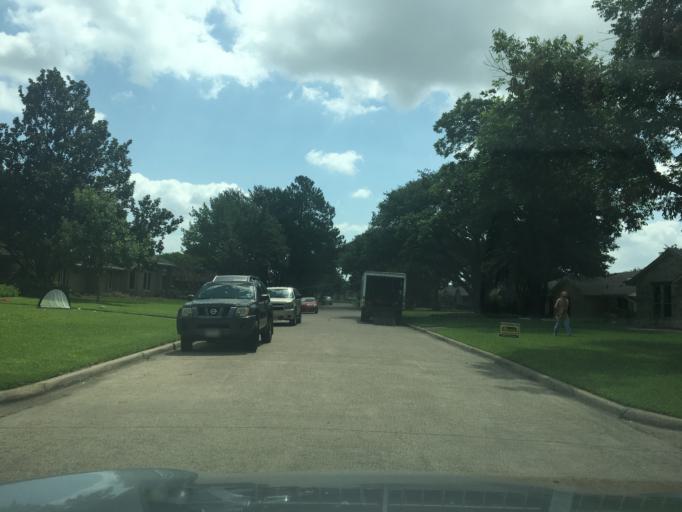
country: US
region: Texas
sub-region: Dallas County
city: Addison
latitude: 32.9215
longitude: -96.8317
